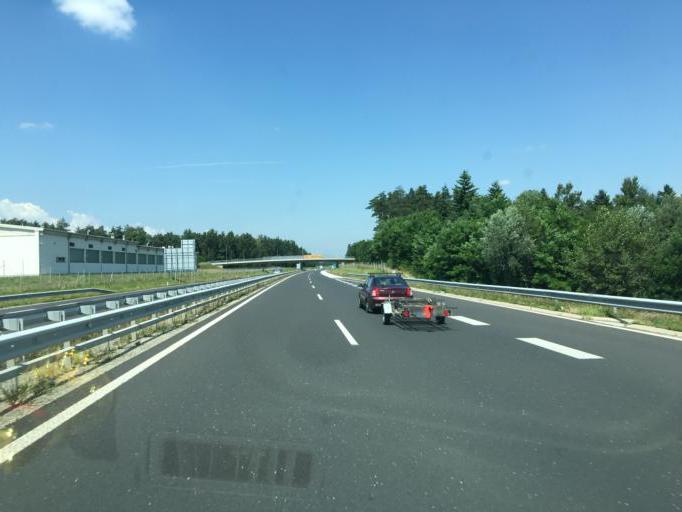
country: SI
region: Kidricevo
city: Kidricevo
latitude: 46.4128
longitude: 15.8100
